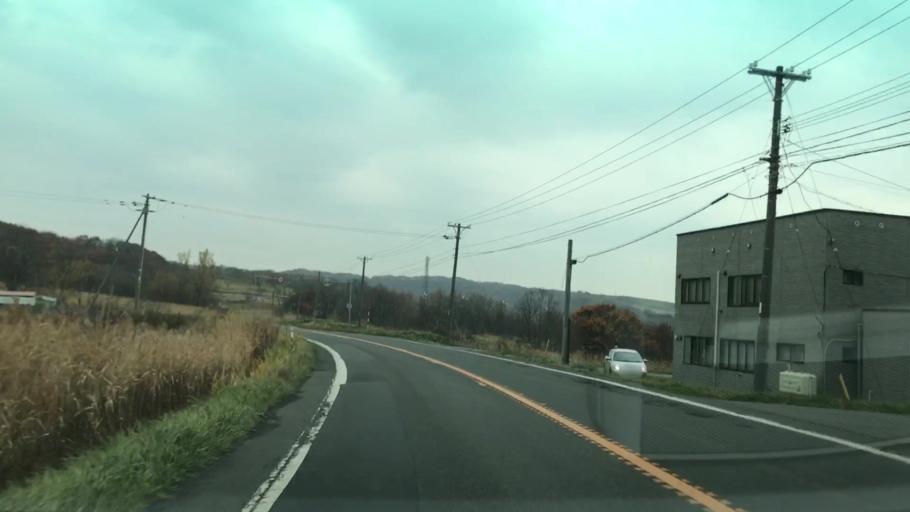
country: JP
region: Hokkaido
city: Ishikari
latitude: 43.3652
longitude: 141.4282
